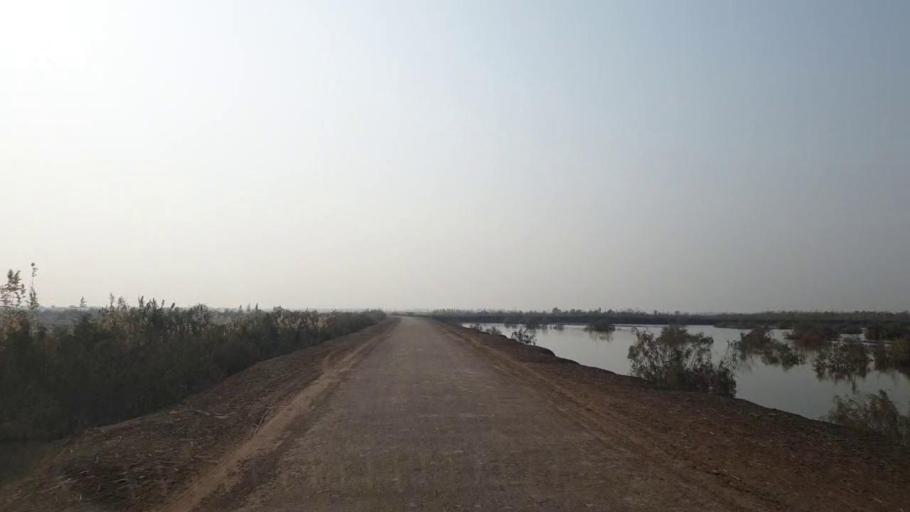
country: PK
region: Sindh
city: Shahdadpur
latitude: 25.9700
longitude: 68.5179
